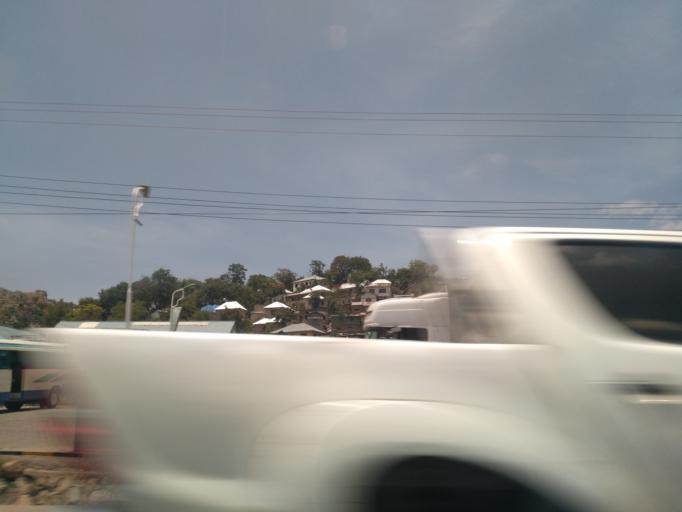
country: TZ
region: Mwanza
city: Mwanza
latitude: -2.5577
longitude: 32.9111
